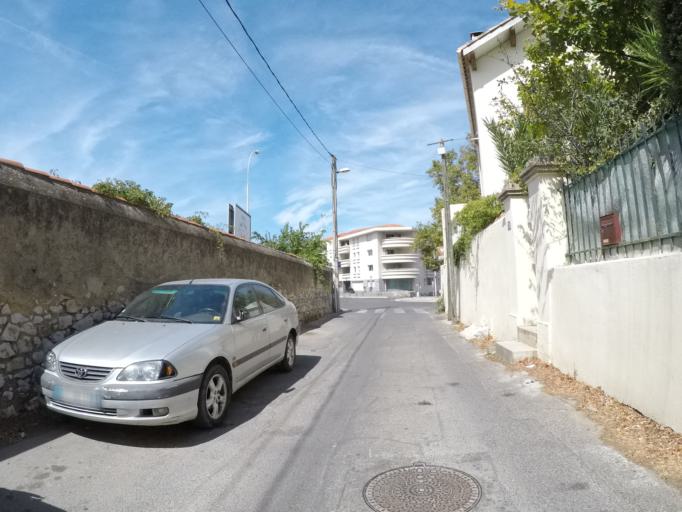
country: FR
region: Provence-Alpes-Cote d'Azur
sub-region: Departement des Bouches-du-Rhone
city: Marseille 08
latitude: 43.2468
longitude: 5.3827
